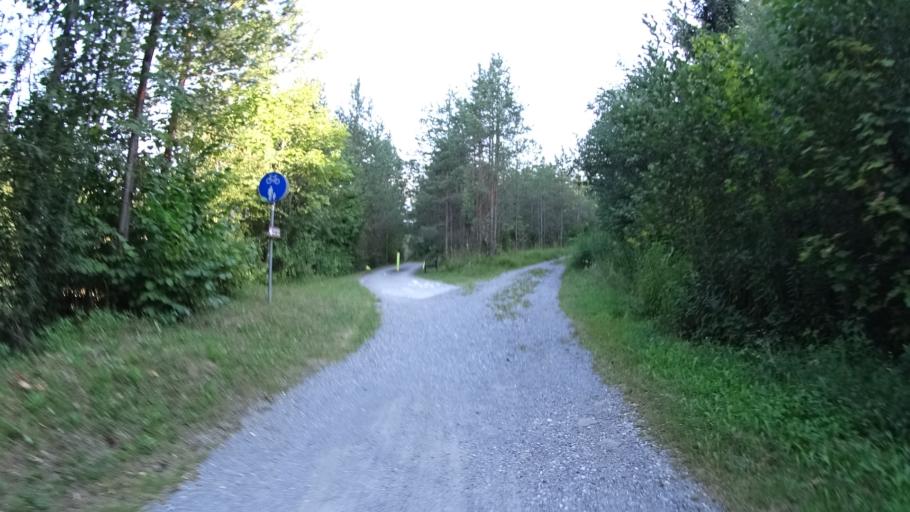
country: AT
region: Carinthia
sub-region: Politischer Bezirk Villach Land
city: Rosegg
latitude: 46.5754
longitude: 14.0208
